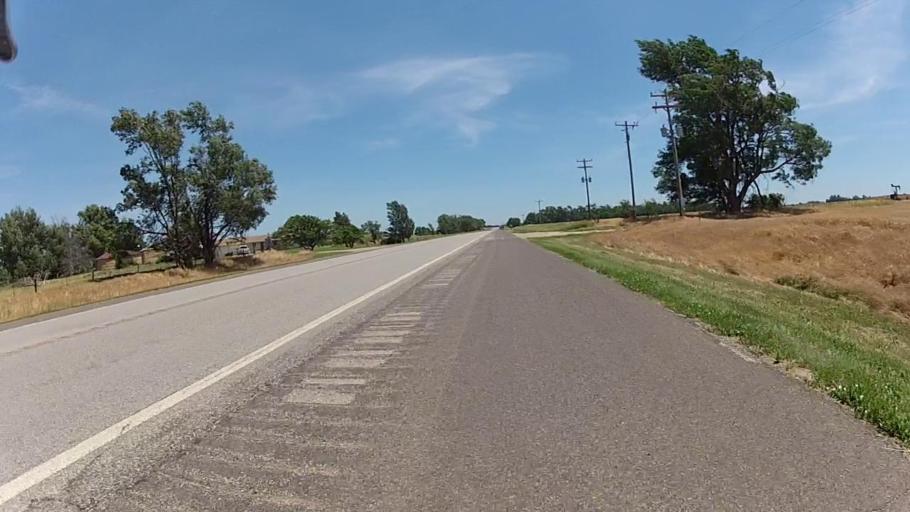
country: US
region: Kansas
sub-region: Barber County
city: Medicine Lodge
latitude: 37.2536
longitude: -98.3769
